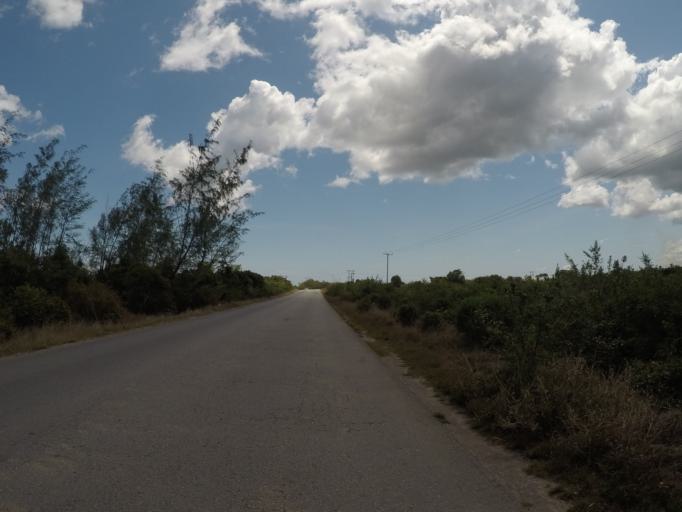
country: TZ
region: Zanzibar Central/South
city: Nganane
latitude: -6.2727
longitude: 39.4944
